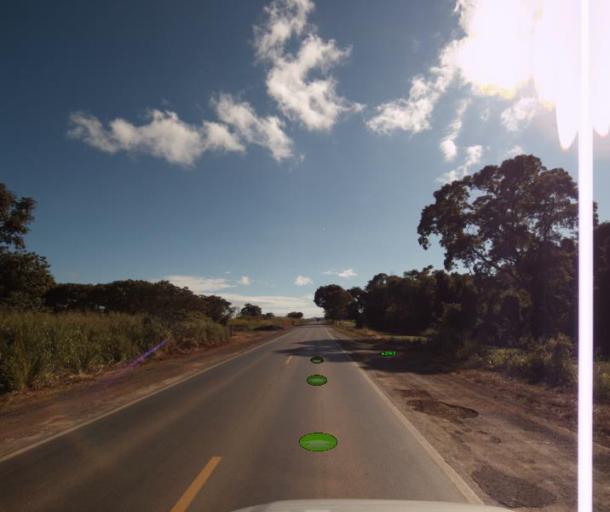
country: BR
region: Goias
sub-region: Uruacu
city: Uruacu
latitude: -14.6482
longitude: -49.1848
